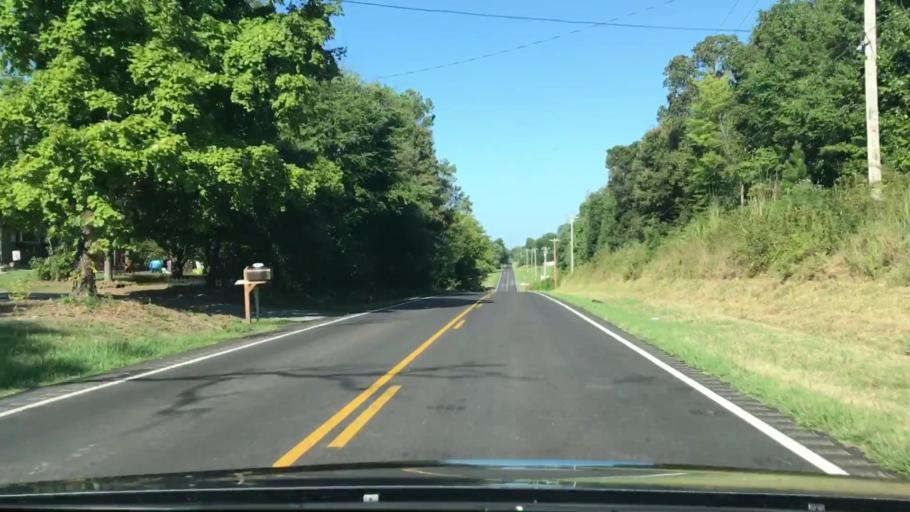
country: US
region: Kentucky
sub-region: Marshall County
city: Benton
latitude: 36.7647
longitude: -88.3233
